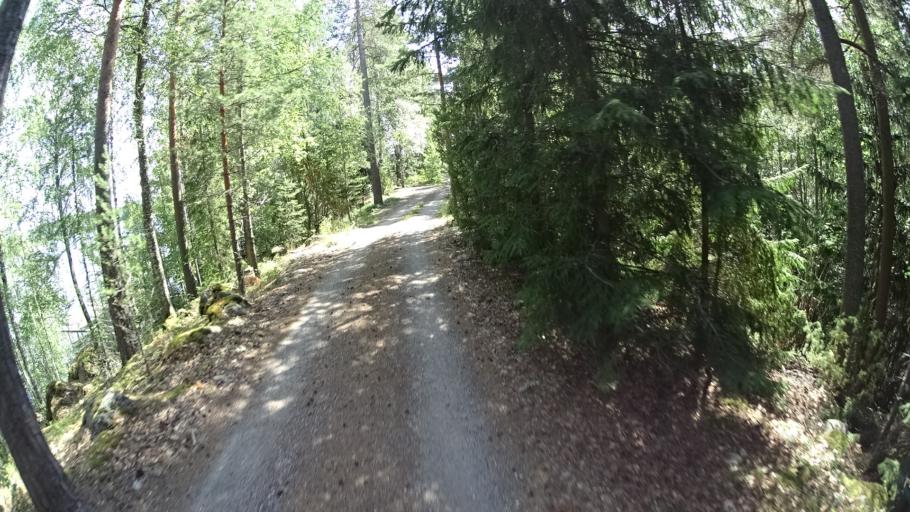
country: FI
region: Haeme
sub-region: Forssa
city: Tammela
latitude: 60.7667
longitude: 23.8870
